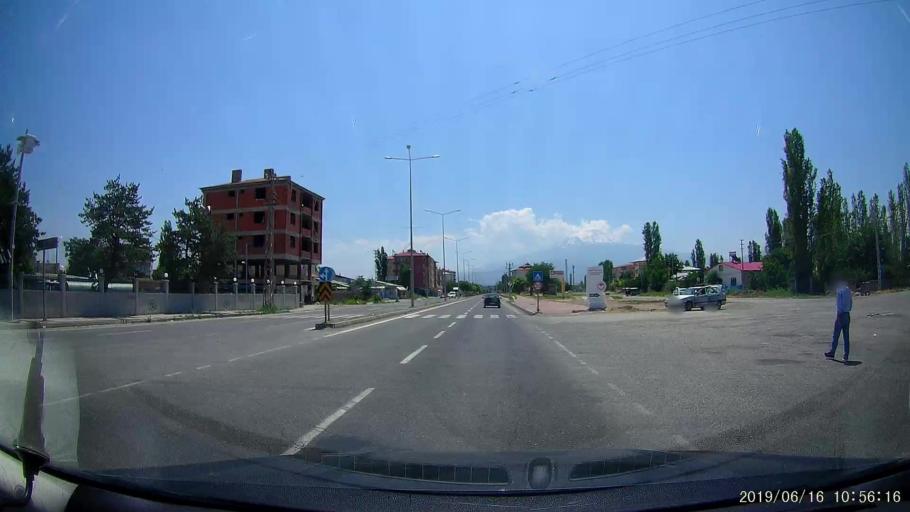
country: TR
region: Igdir
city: Igdir
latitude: 39.9309
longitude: 44.0203
